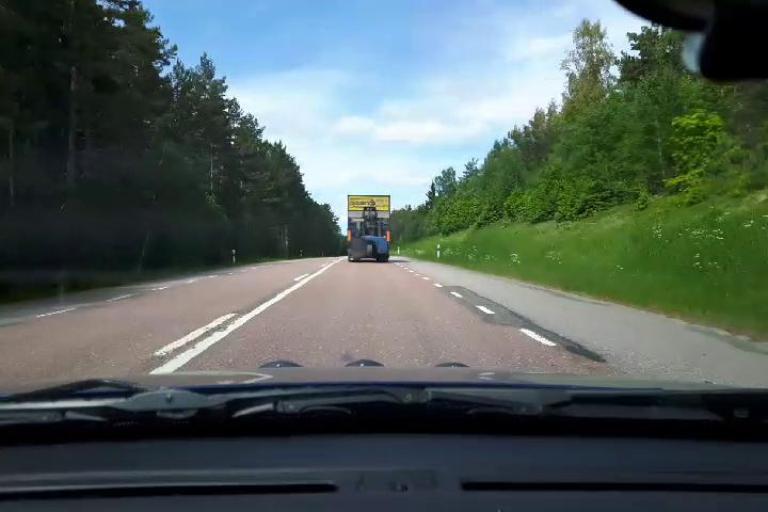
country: SE
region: Uppsala
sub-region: Osthammars Kommun
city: Bjorklinge
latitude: 60.1376
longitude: 17.5061
